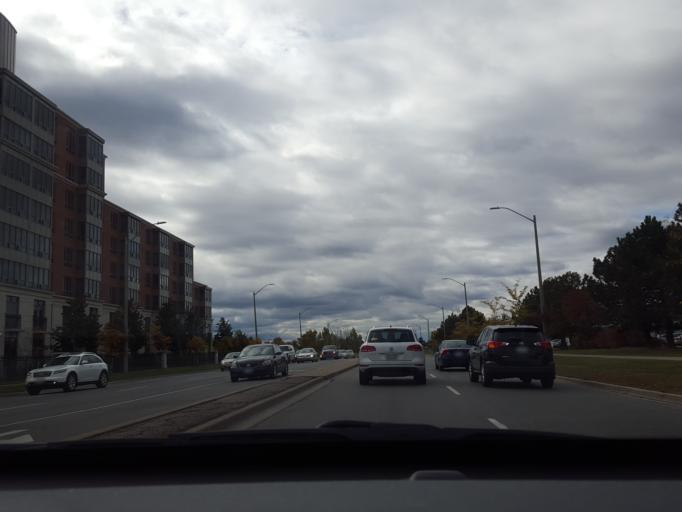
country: CA
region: Ontario
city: Markham
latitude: 43.8343
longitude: -79.3045
